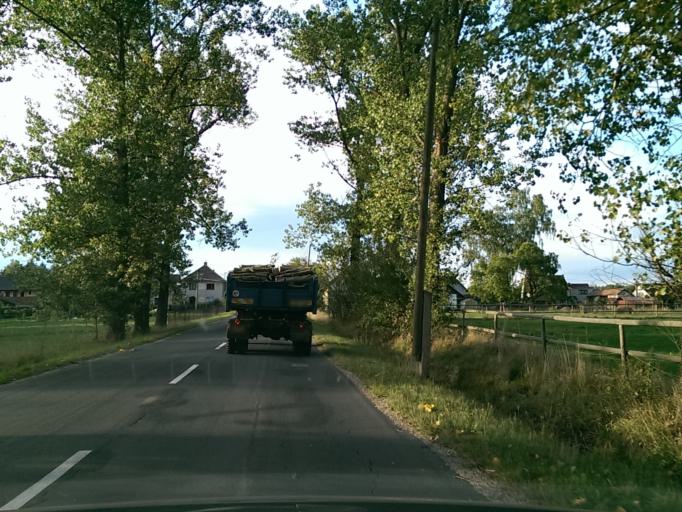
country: CZ
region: Central Bohemia
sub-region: Okres Mlada Boleslav
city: Zd'ar
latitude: 50.5284
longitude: 15.1017
